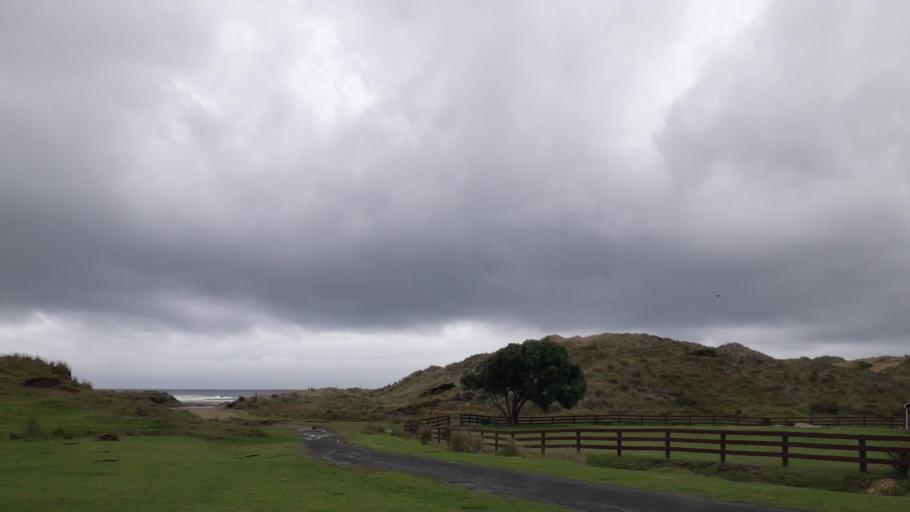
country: NZ
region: Northland
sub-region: Far North District
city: Ahipara
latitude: -35.4399
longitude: 173.2857
